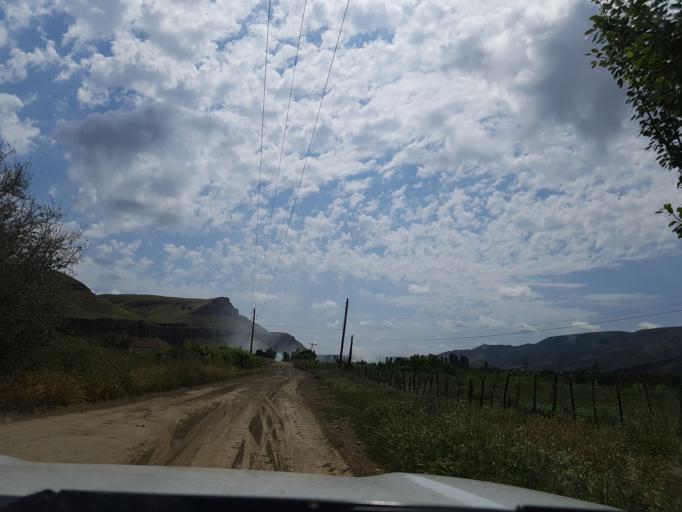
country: TM
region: Ahal
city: Baharly
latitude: 38.2267
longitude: 56.8744
